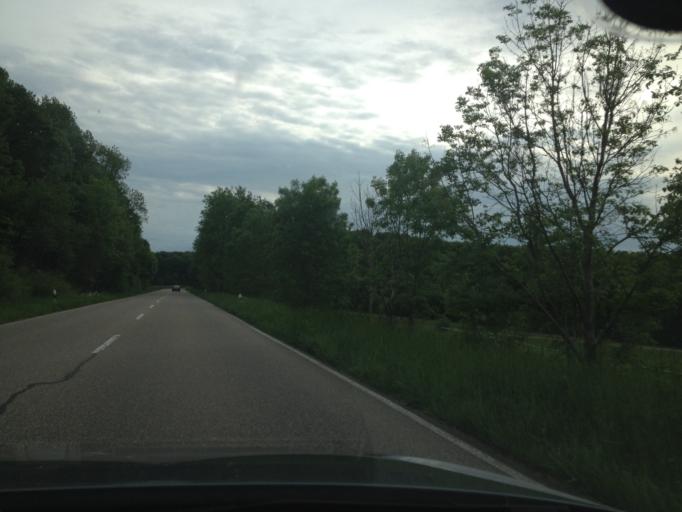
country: DE
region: Rheinland-Pfalz
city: Hoheischweiler
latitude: 49.2274
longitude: 7.5445
